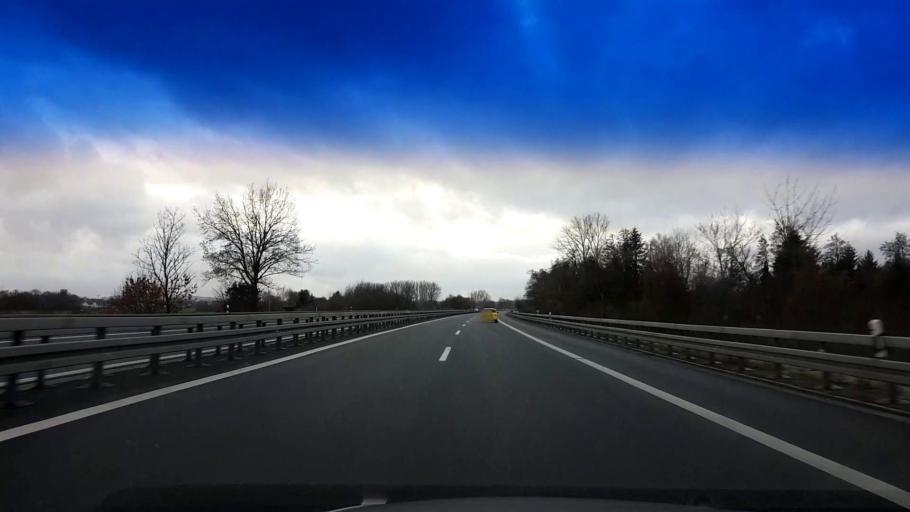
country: DE
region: Bavaria
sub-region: Upper Franconia
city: Memmelsdorf
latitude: 49.9351
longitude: 10.9443
